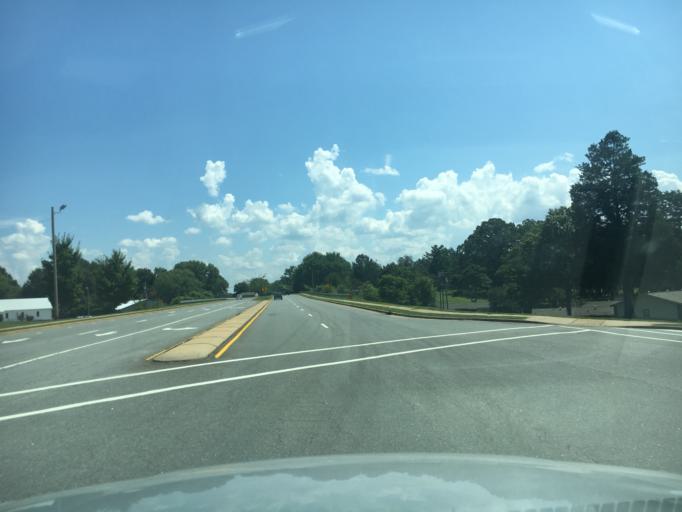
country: US
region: North Carolina
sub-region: Rutherford County
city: Forest City
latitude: 35.3298
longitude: -81.8660
